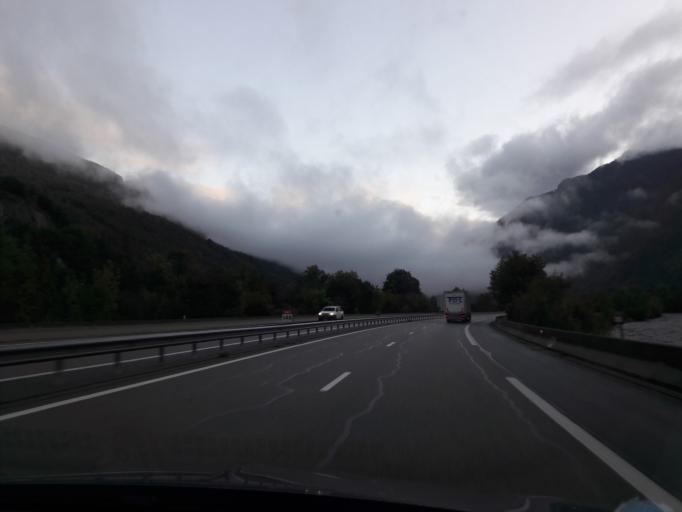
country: FR
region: Rhone-Alpes
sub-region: Departement de la Savoie
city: Saint-Remy-de-Maurienne
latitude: 45.4328
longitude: 6.2777
